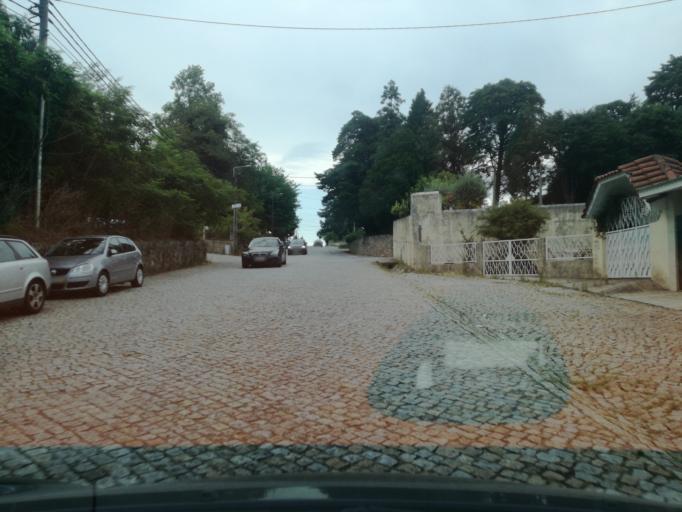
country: PT
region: Porto
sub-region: Maia
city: Leca do Bailio
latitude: 41.2276
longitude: -8.6052
